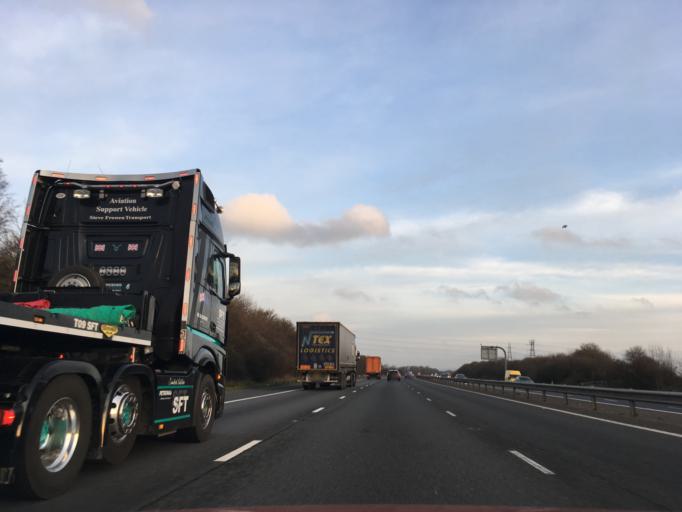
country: GB
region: England
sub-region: Gloucestershire
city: Uckington
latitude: 51.9136
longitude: -2.1507
